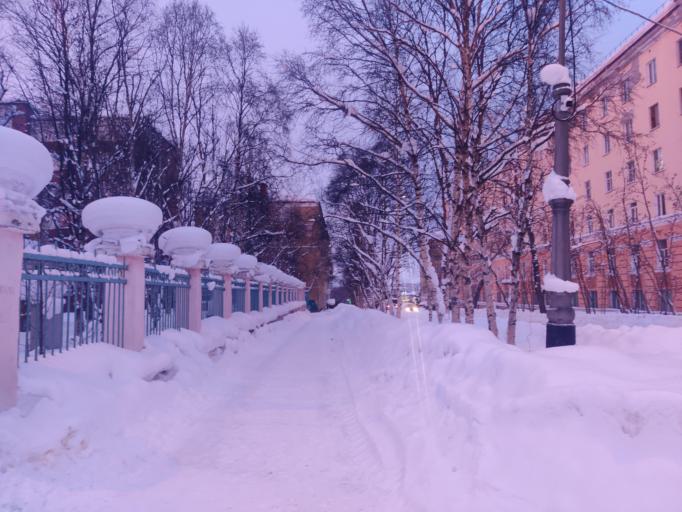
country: RU
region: Murmansk
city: Murmansk
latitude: 68.9766
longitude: 33.0824
